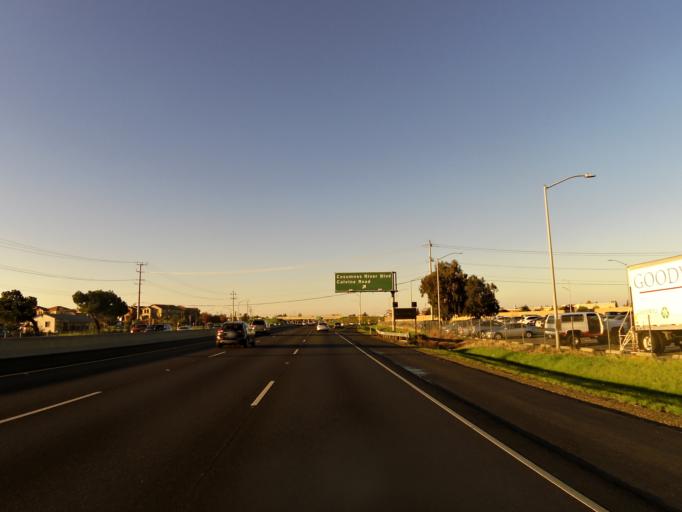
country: US
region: California
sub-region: Sacramento County
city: Laguna
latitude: 38.4515
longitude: -121.4078
